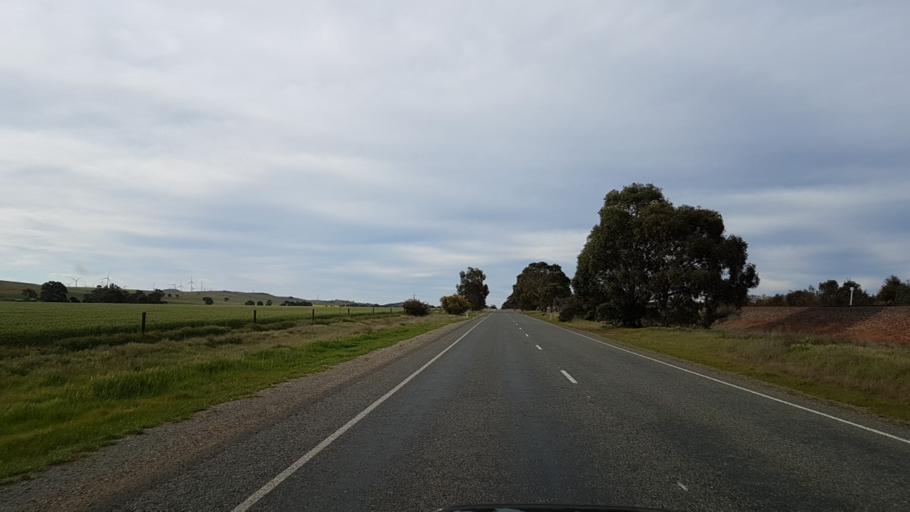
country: AU
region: South Australia
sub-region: Northern Areas
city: Jamestown
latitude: -33.1773
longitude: 138.6117
